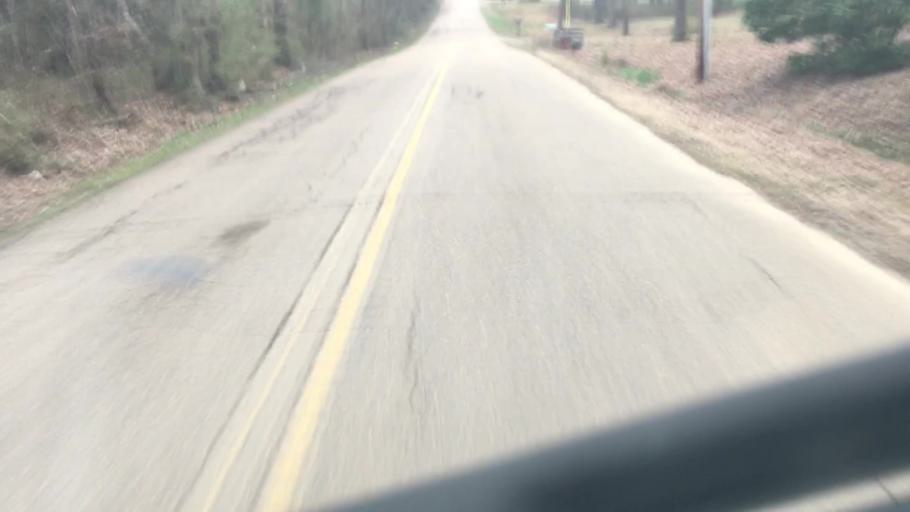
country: US
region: Alabama
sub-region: Walker County
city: Jasper
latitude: 33.8311
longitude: -87.2253
